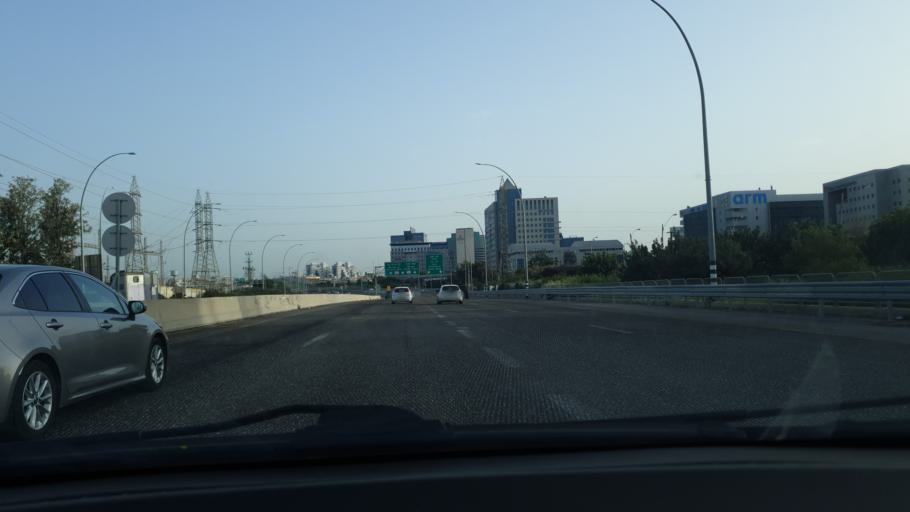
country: IL
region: Central District
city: Ra'anana
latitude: 32.2009
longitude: 34.8845
